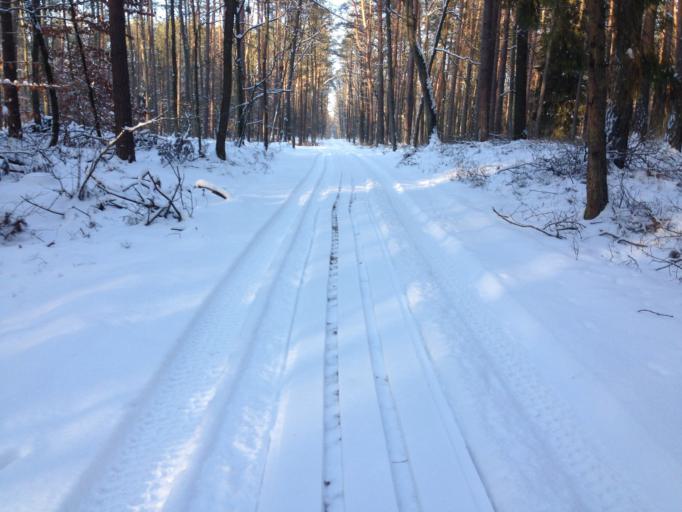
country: PL
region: Kujawsko-Pomorskie
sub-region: Powiat brodnicki
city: Gorzno
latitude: 53.1938
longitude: 19.6904
